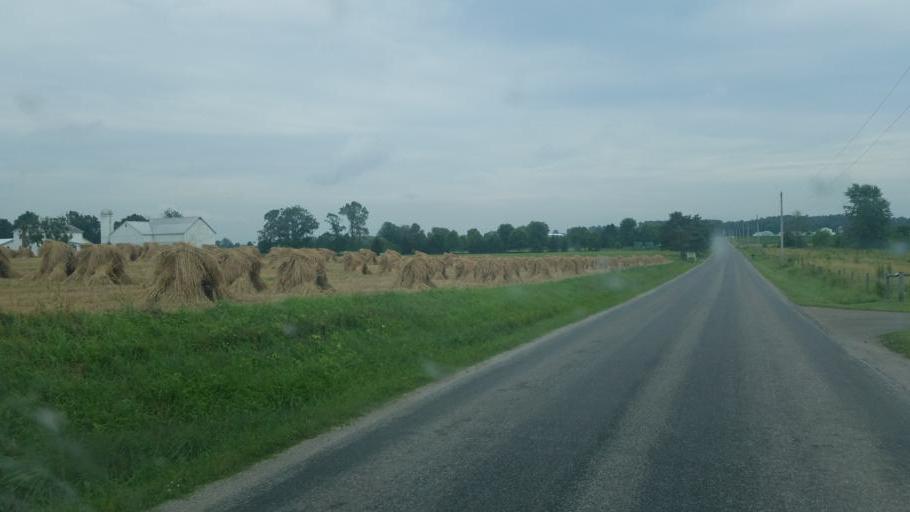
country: US
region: Ohio
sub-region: Wayne County
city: Apple Creek
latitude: 40.7659
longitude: -81.7752
